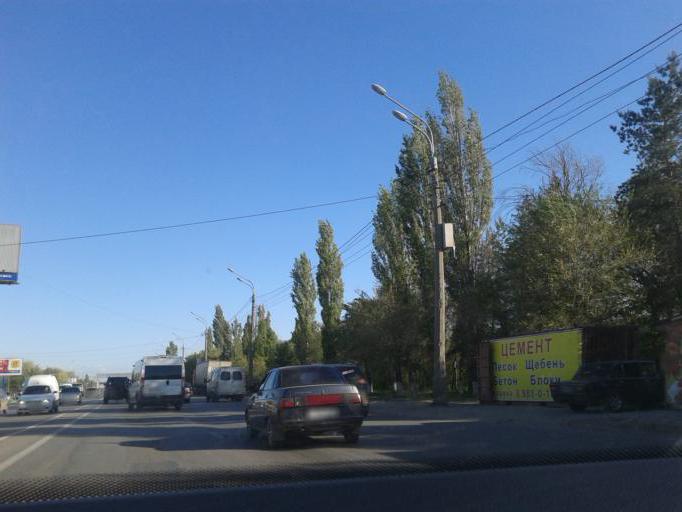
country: RU
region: Volgograd
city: Gorodishche
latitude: 48.7611
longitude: 44.4775
